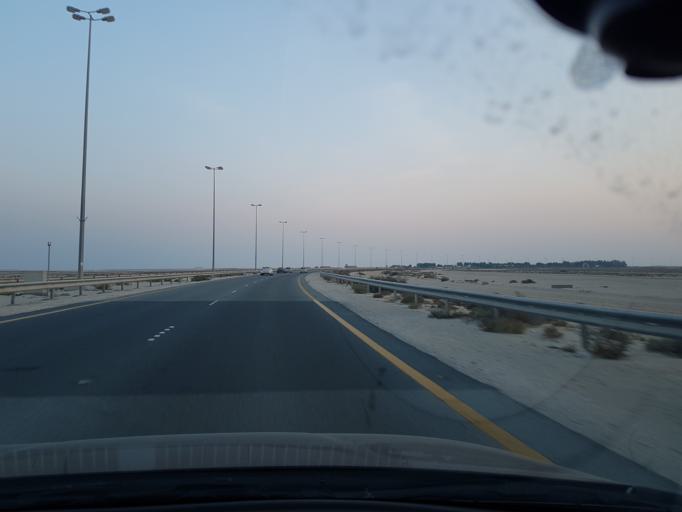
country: BH
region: Central Governorate
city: Dar Kulayb
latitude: 26.0004
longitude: 50.4851
